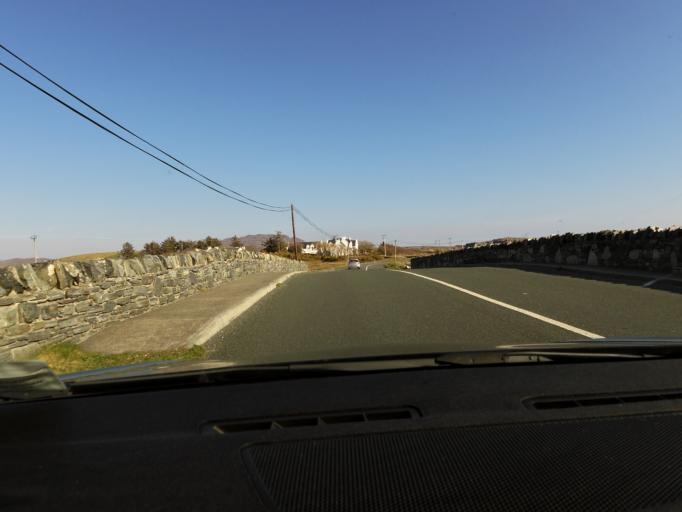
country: IE
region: Connaught
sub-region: County Galway
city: Clifden
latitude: 53.4095
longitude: -10.0368
